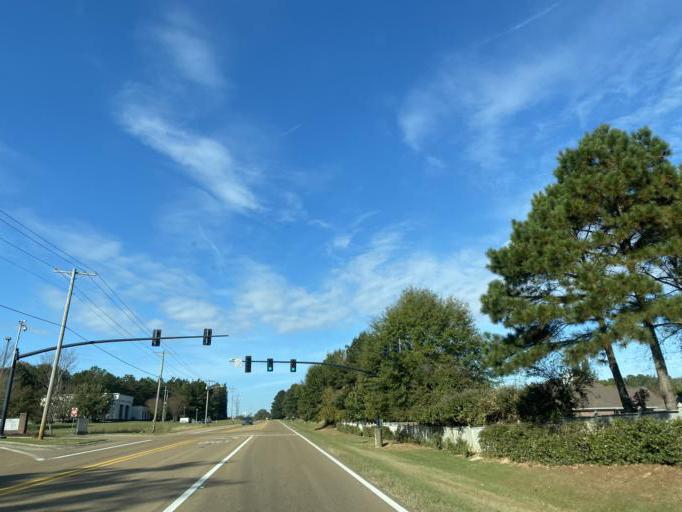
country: US
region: Mississippi
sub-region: Madison County
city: Madison
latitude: 32.4808
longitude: -90.1662
